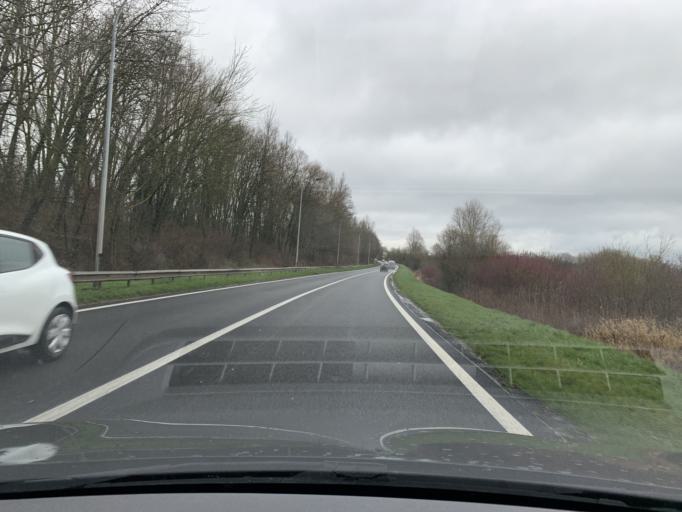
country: FR
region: Nord-Pas-de-Calais
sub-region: Departement du Nord
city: Sin-le-Noble
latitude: 50.3738
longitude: 3.1227
